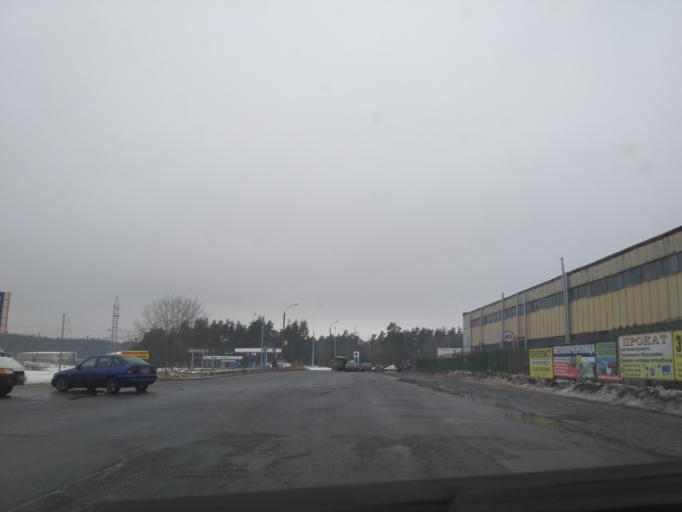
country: BY
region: Minsk
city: Horad Barysaw
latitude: 54.1994
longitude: 28.4880
